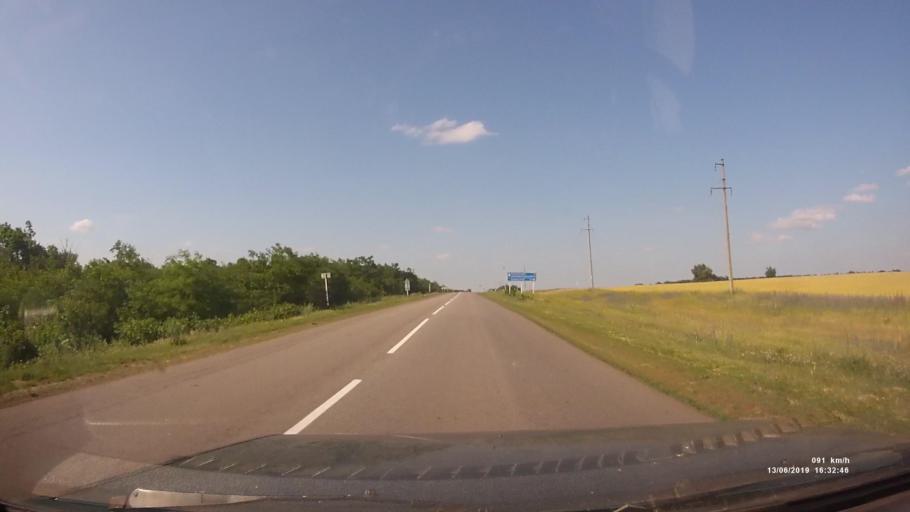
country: RU
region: Rostov
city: Kazanskaya
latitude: 49.8522
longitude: 41.2740
